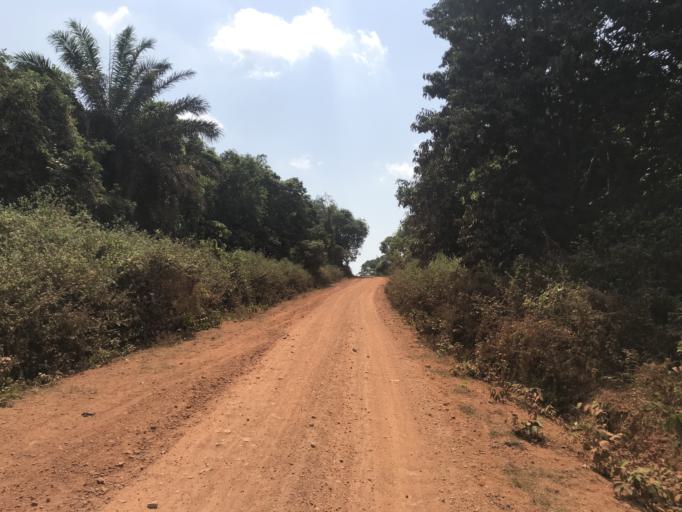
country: NG
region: Osun
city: Ifon
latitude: 7.9623
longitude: 4.4983
